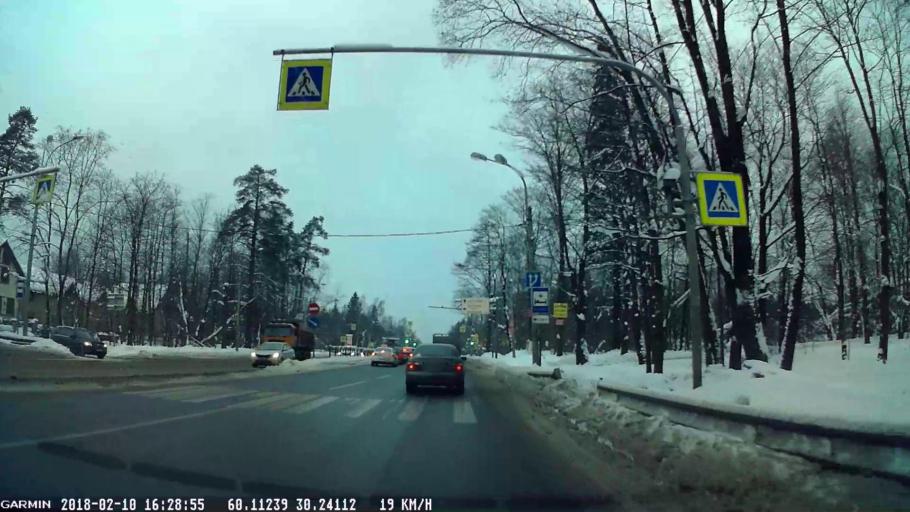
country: RU
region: St.-Petersburg
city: Levashovo
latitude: 60.1126
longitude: 30.2410
